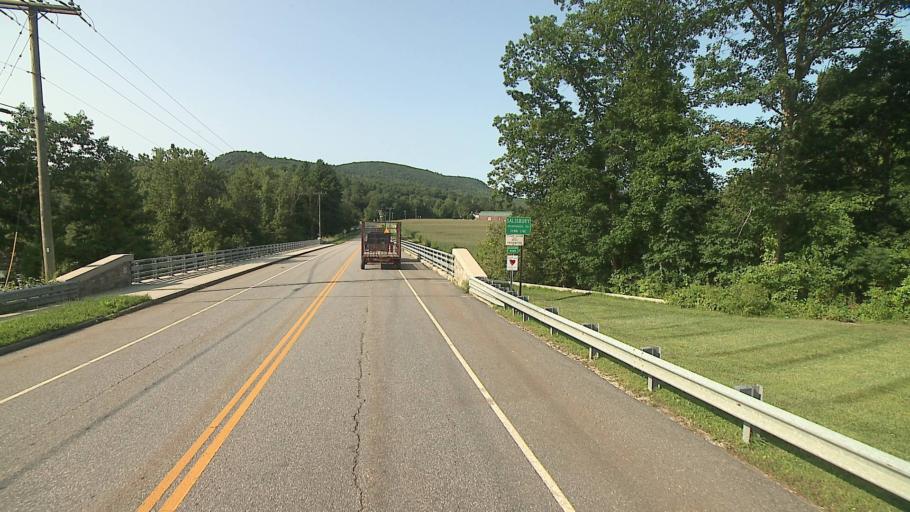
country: US
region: Connecticut
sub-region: Litchfield County
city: Canaan
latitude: 41.9349
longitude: -73.3614
